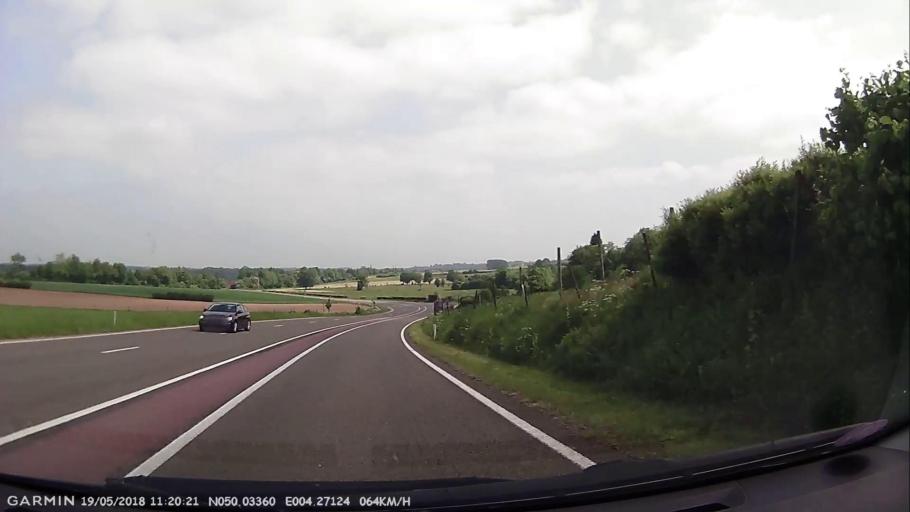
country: BE
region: Wallonia
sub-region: Province du Hainaut
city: Chimay
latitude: 50.0337
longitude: 4.2717
